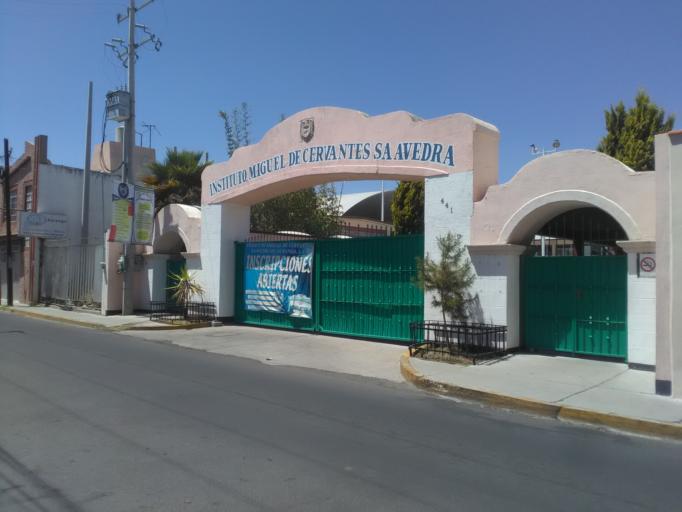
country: MX
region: Durango
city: Victoria de Durango
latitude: 24.0312
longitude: -104.6602
